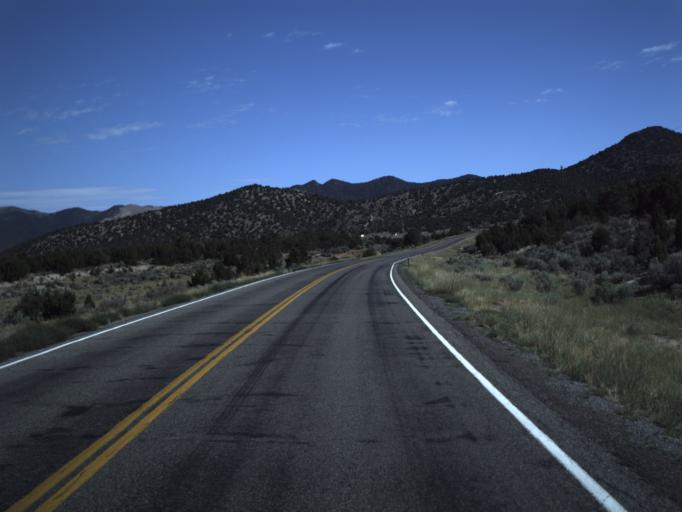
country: US
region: Utah
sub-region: Utah County
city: Genola
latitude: 39.9337
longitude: -112.1493
